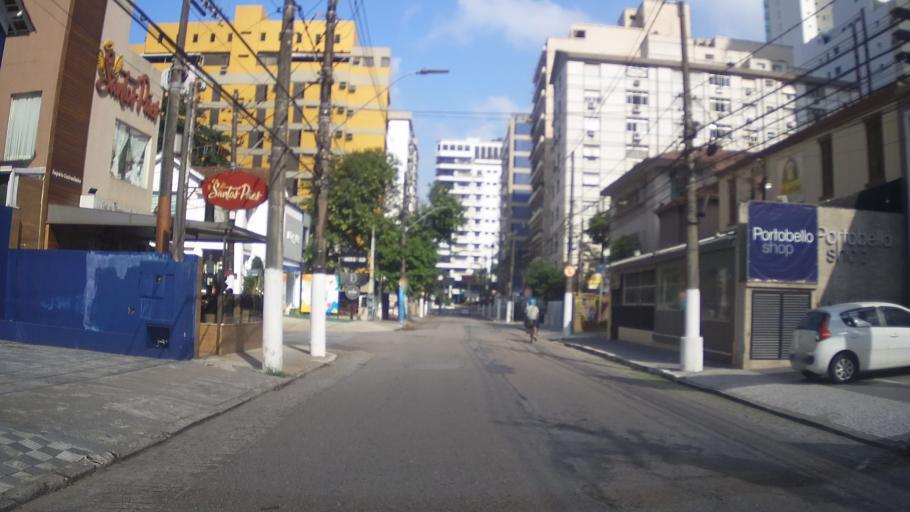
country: BR
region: Sao Paulo
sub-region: Santos
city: Santos
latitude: -23.9663
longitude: -46.3270
